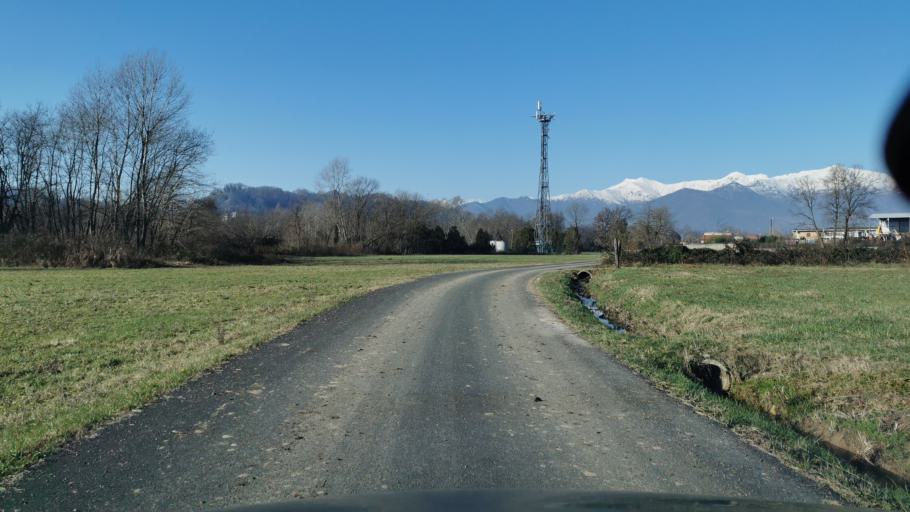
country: IT
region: Piedmont
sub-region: Provincia di Torino
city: Front
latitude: 45.2814
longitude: 7.6750
